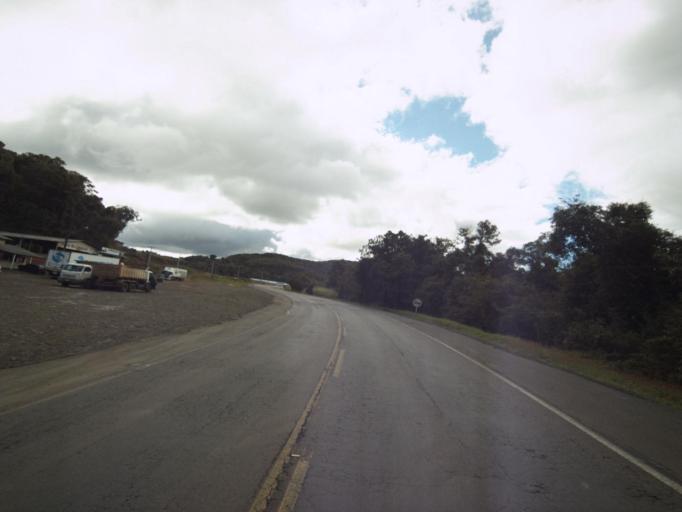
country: BR
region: Santa Catarina
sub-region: Concordia
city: Concordia
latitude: -27.2058
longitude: -51.9495
